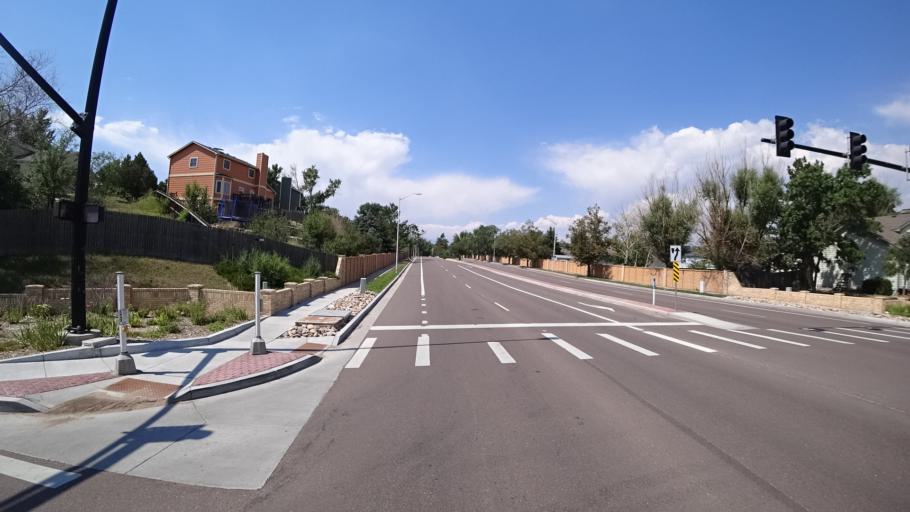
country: US
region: Colorado
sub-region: El Paso County
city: Cimarron Hills
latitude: 38.9258
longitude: -104.7563
